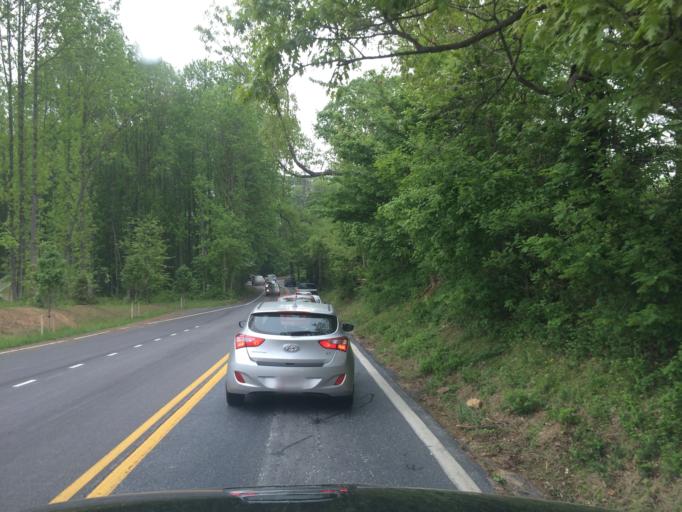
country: US
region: Maryland
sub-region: Howard County
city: Columbia
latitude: 39.2911
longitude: -76.9025
